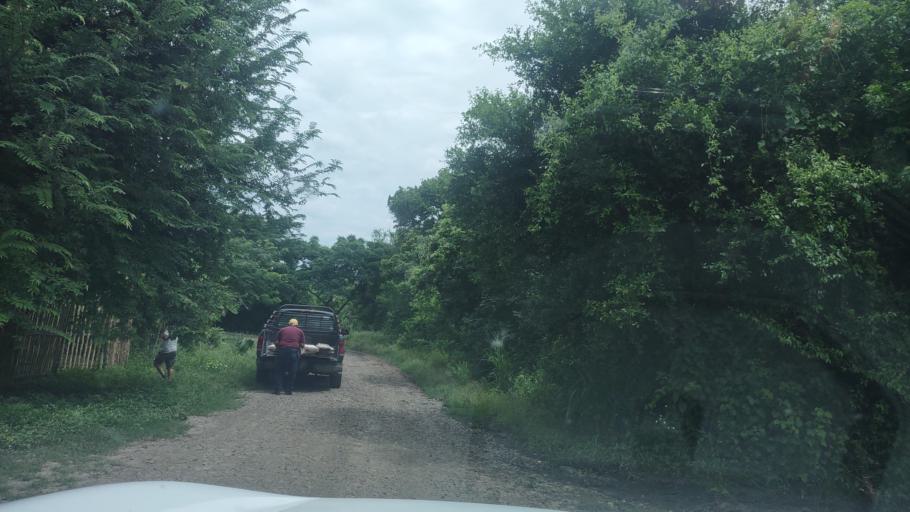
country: MX
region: Veracruz
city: Tepetzintla
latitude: 21.0463
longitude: -97.9979
